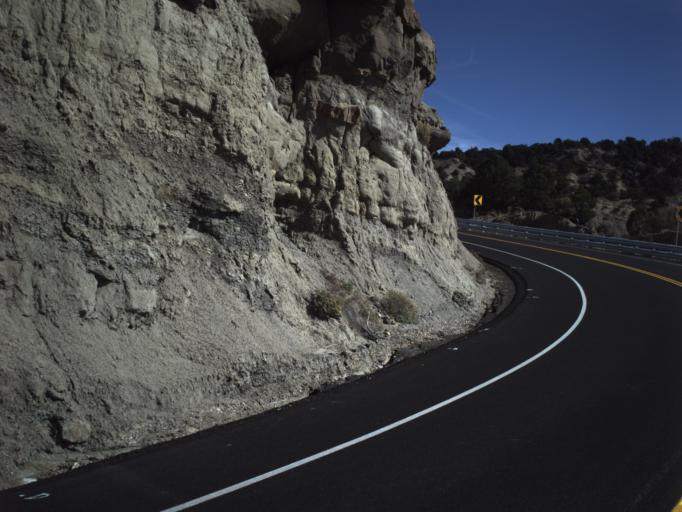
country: US
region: Utah
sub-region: Garfield County
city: Panguitch
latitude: 37.6361
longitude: -111.8427
